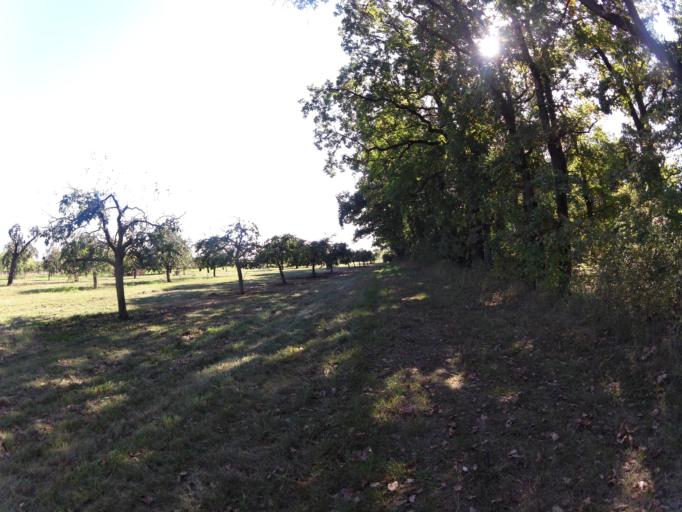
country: DE
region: Bavaria
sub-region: Regierungsbezirk Unterfranken
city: Sommerhausen
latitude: 49.6923
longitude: 10.0377
